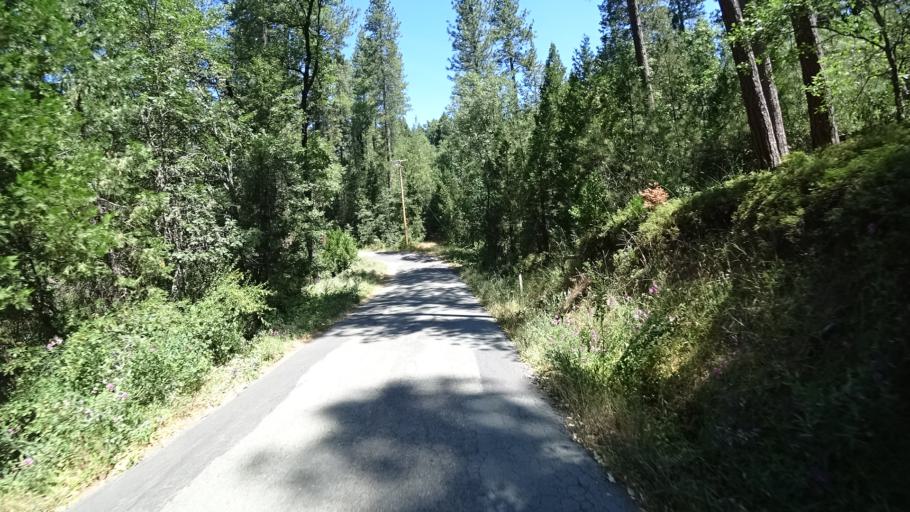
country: US
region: California
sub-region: Amador County
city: Pioneer
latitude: 38.4066
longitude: -120.5226
